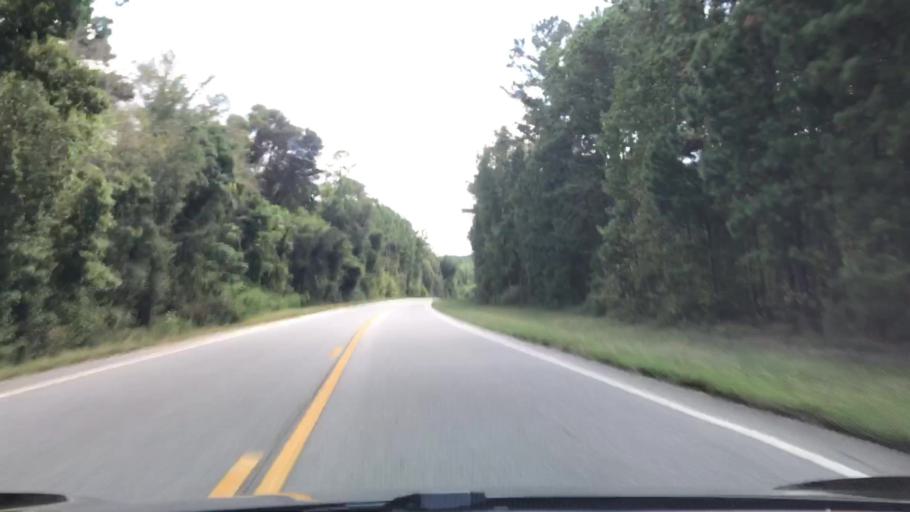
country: US
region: Georgia
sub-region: Greene County
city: Greensboro
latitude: 33.6968
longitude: -83.2788
